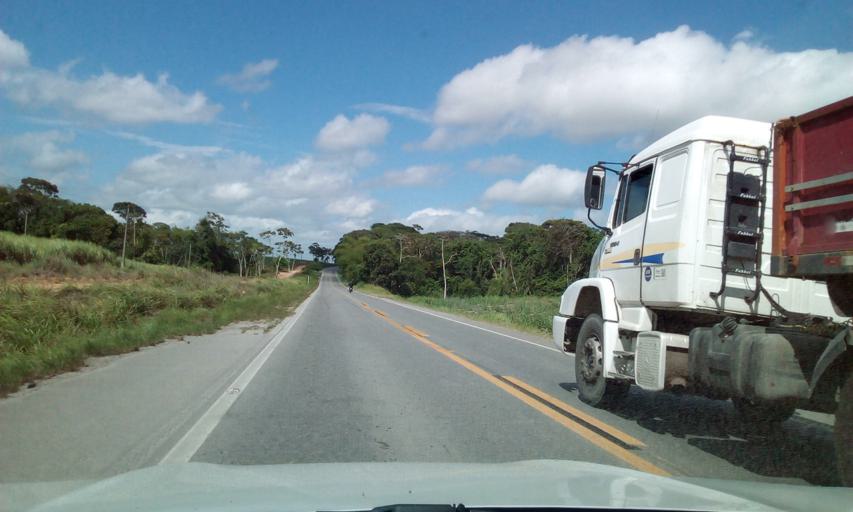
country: BR
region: Alagoas
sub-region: Pilar
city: Pilar
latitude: -9.5175
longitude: -35.9357
